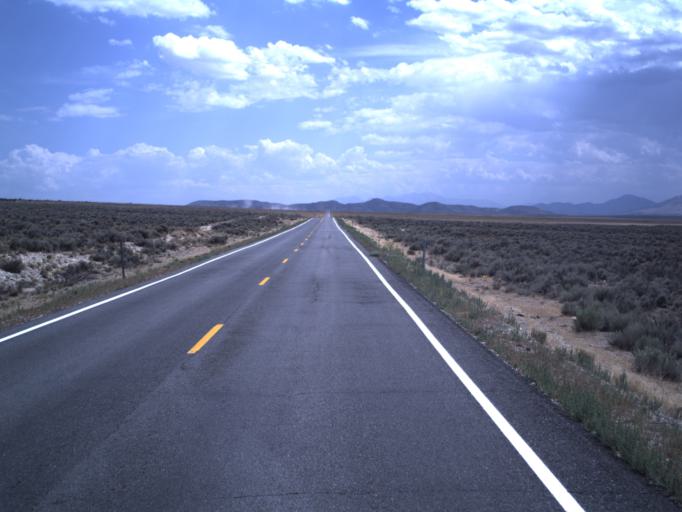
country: US
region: Utah
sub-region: Utah County
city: Eagle Mountain
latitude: 40.2784
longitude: -112.2548
